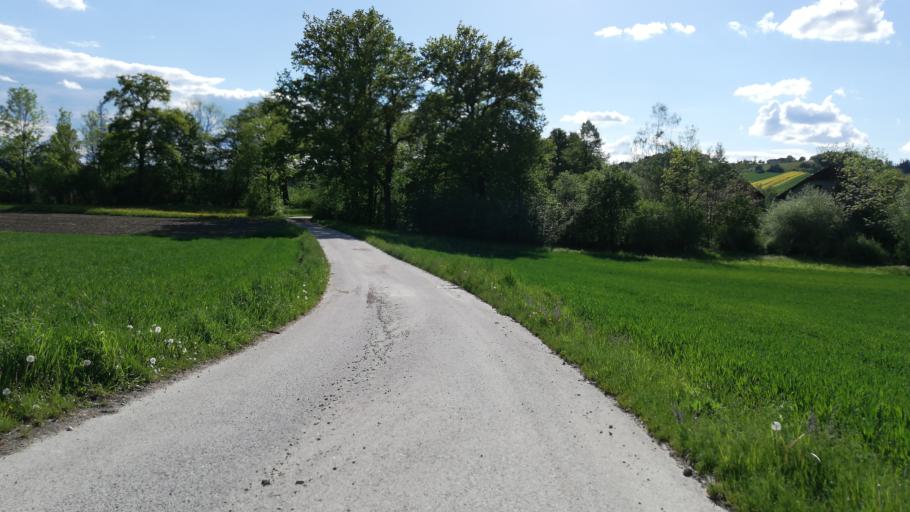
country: AT
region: Upper Austria
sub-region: Politischer Bezirk Grieskirchen
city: Bad Schallerbach
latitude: 48.2086
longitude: 13.9336
